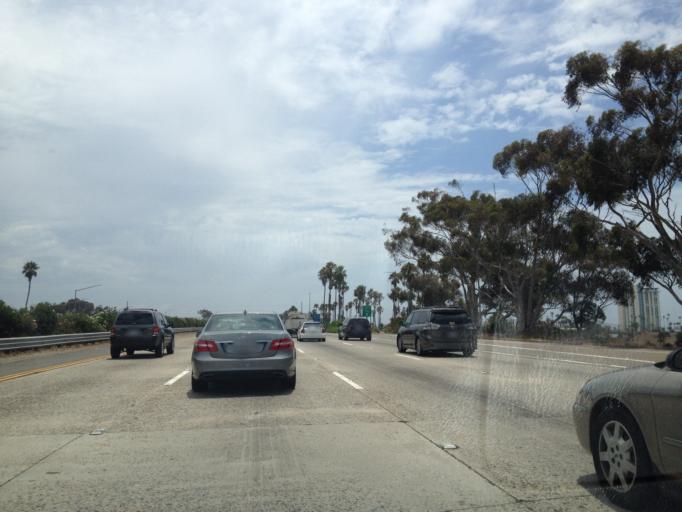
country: US
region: California
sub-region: San Diego County
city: Camp Pendleton South
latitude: 33.2133
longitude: -117.3892
